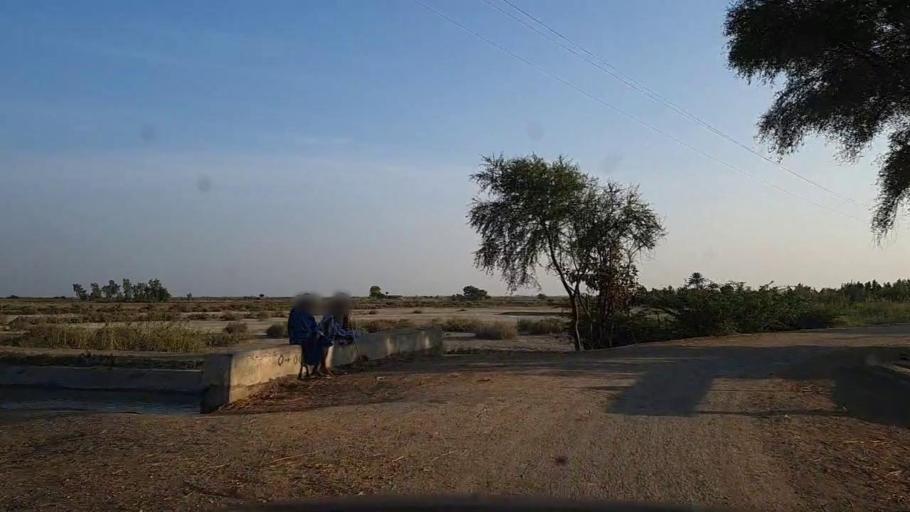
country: PK
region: Sindh
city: Thatta
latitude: 24.6250
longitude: 67.9148
